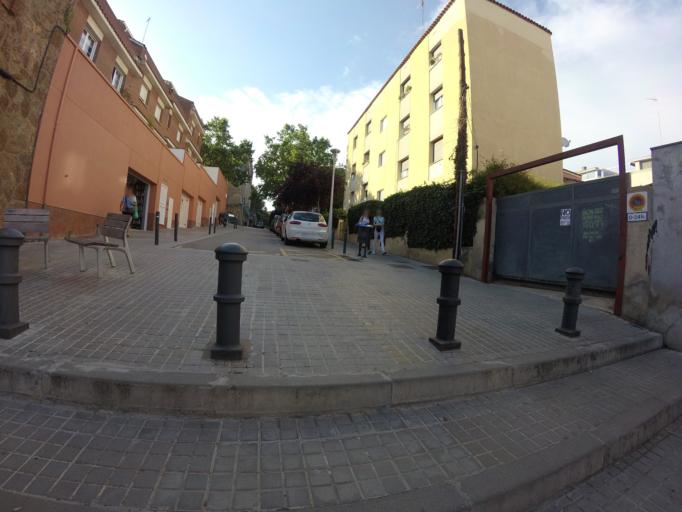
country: ES
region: Catalonia
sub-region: Provincia de Barcelona
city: Gracia
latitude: 41.4113
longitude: 2.1533
